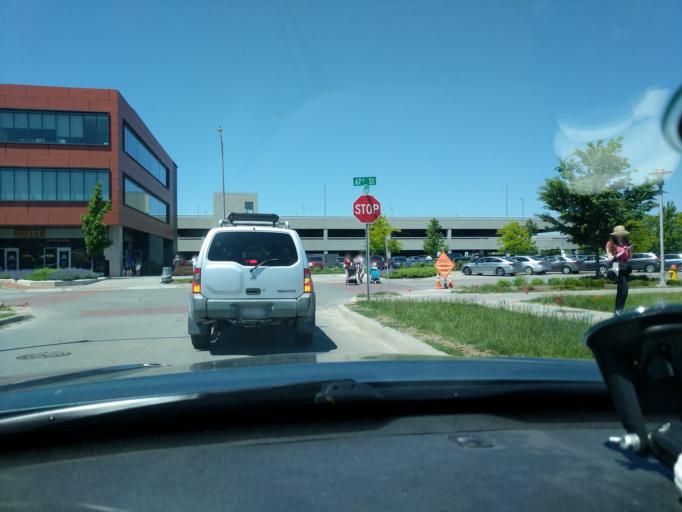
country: US
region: Nebraska
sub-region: Douglas County
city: Ralston
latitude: 41.2415
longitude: -96.0142
